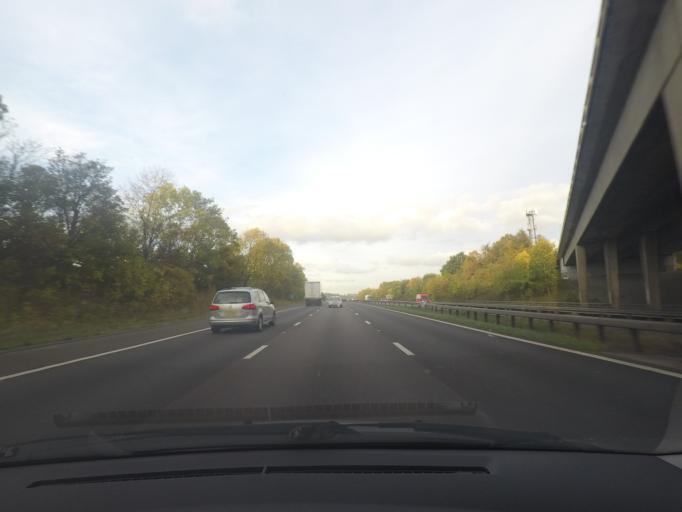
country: GB
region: England
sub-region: City and Borough of Wakefield
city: Crigglestone
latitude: 53.6399
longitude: -1.5370
